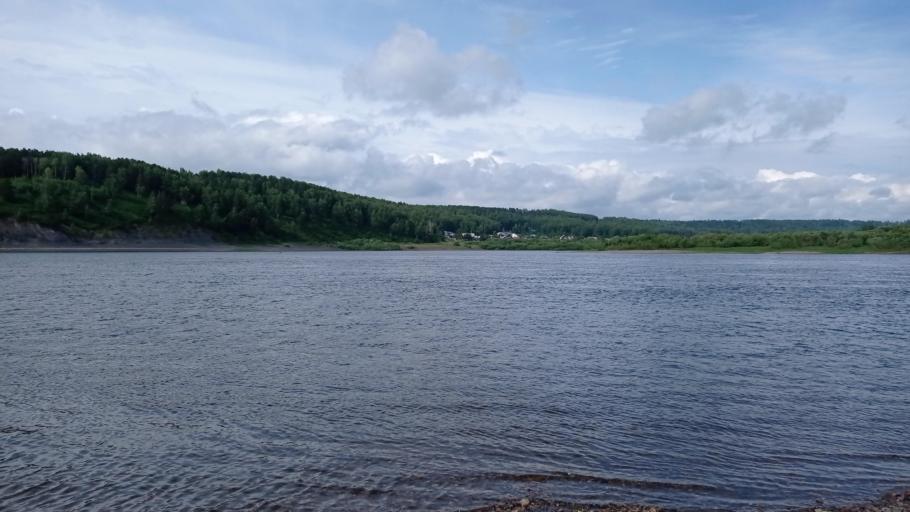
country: RU
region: Tomsk
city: Kaltay
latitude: 56.3274
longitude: 84.9268
